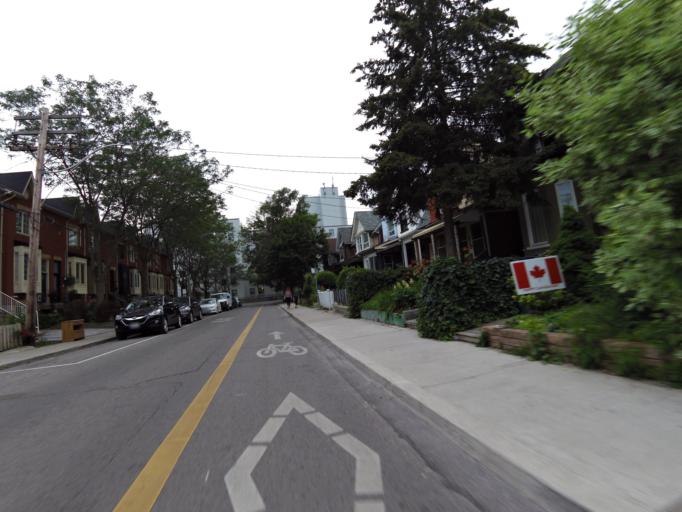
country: CA
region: Ontario
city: Toronto
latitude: 43.6455
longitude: -79.4087
